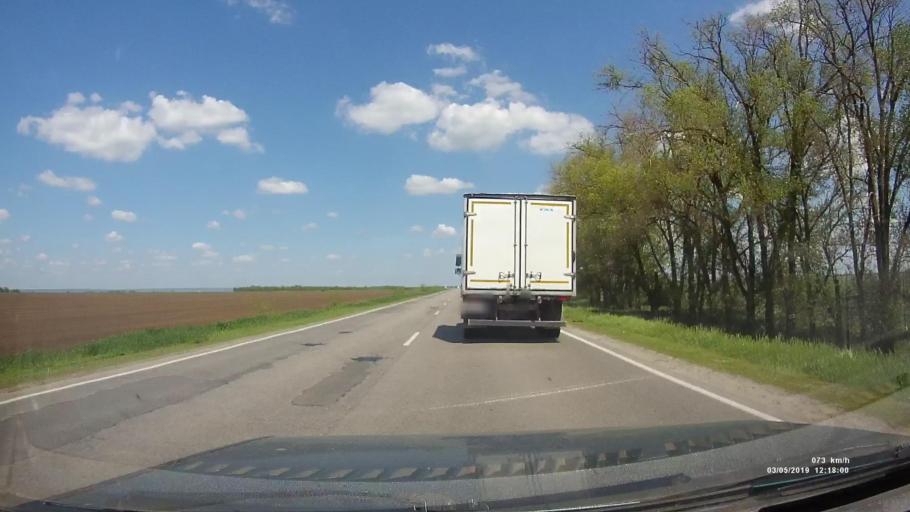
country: RU
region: Rostov
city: Melikhovskaya
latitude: 47.3880
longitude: 40.5963
